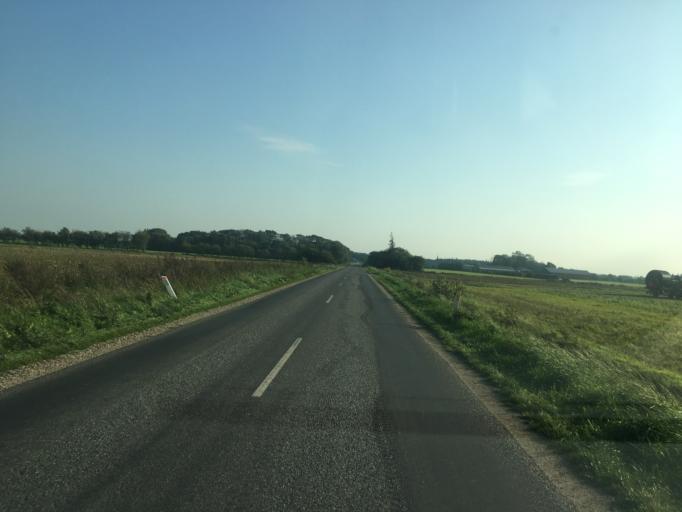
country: DE
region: Schleswig-Holstein
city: Bramstedtlund
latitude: 54.9369
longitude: 9.0670
